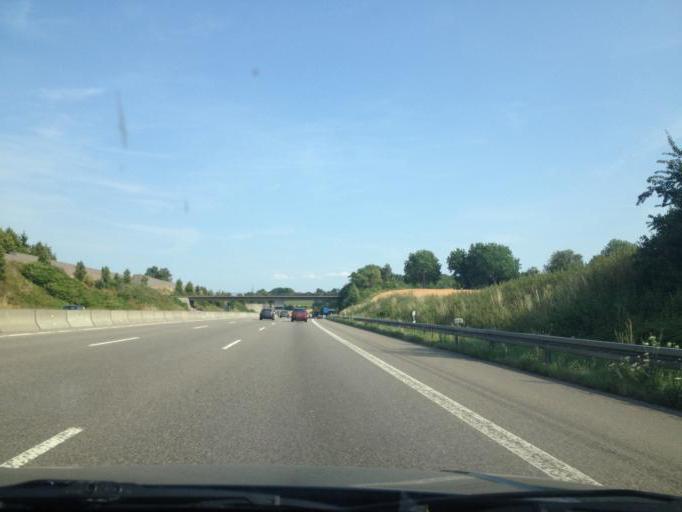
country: DE
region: Baden-Wuerttemberg
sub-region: Karlsruhe Region
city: Sinsheim
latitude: 49.2345
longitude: 8.9010
